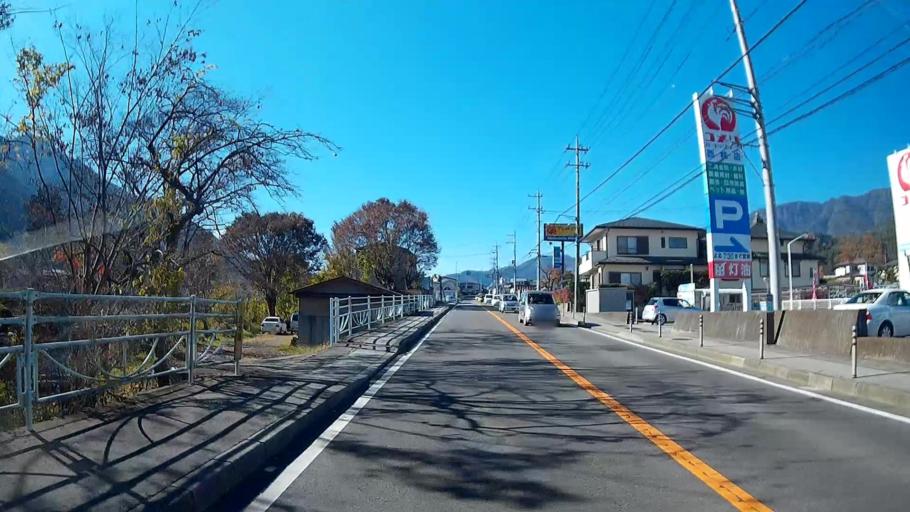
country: JP
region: Yamanashi
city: Otsuki
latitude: 35.5293
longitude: 138.8596
